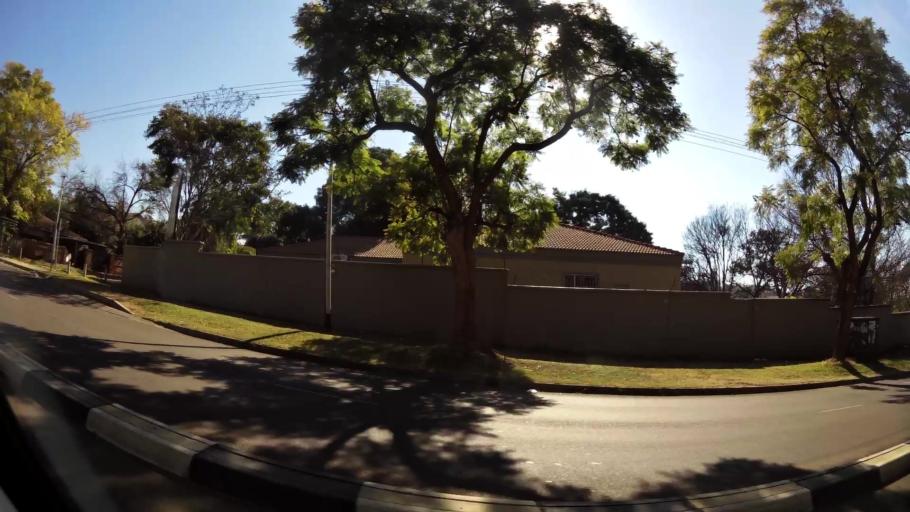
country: ZA
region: Gauteng
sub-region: City of Tshwane Metropolitan Municipality
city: Pretoria
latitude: -25.7742
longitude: 28.2651
